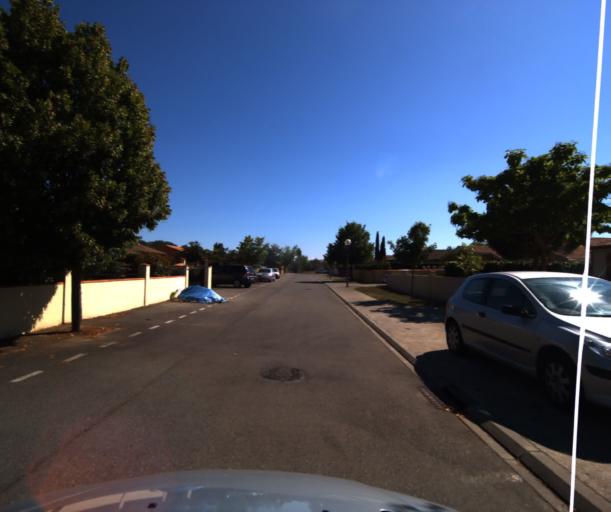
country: FR
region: Midi-Pyrenees
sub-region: Departement de la Haute-Garonne
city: Le Fauga
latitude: 43.4220
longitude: 1.3157
